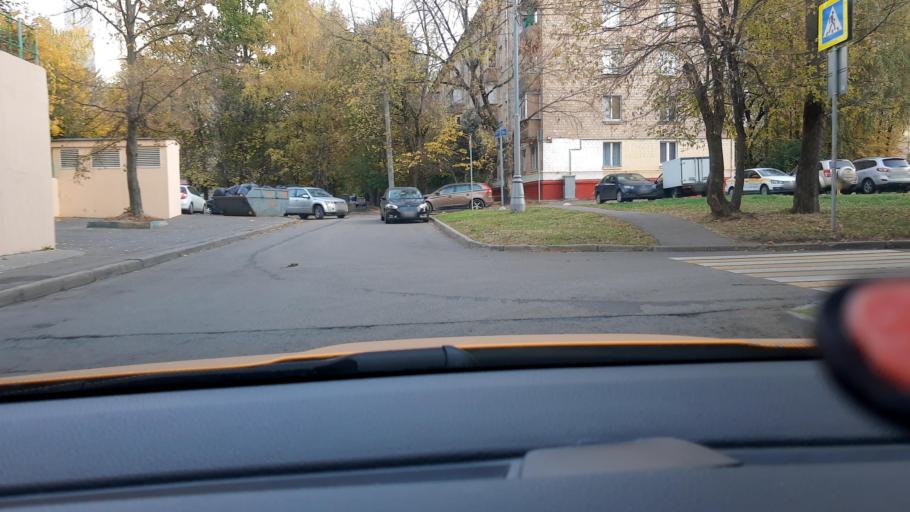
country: RU
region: Moscow
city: Businovo
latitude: 55.8780
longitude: 37.5146
